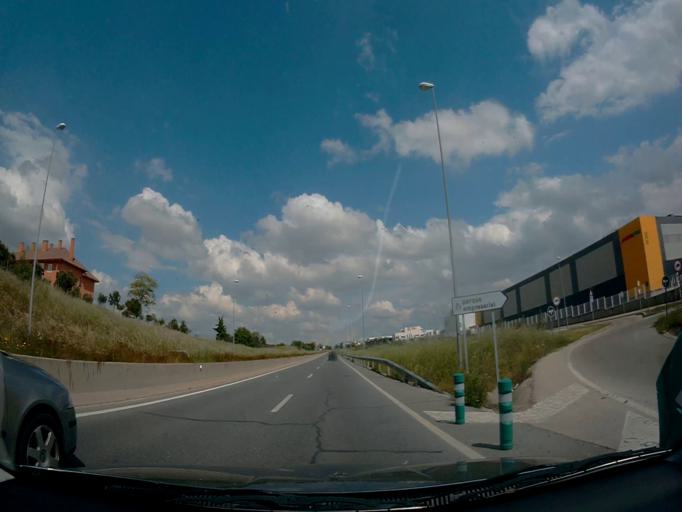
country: ES
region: Madrid
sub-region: Provincia de Madrid
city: Villaviciosa de Odon
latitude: 40.3512
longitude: -3.8999
